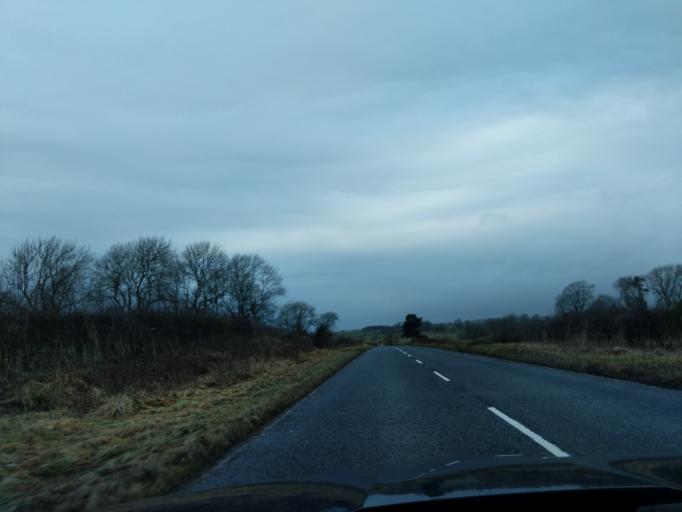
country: GB
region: England
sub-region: Northumberland
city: Rothley
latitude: 55.1506
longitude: -2.0050
